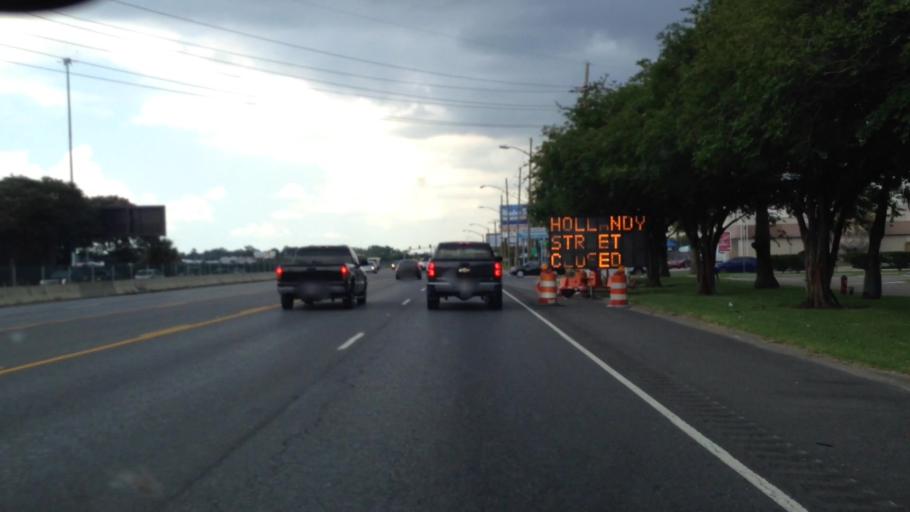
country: US
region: Louisiana
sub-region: Jefferson Parish
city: Kenner
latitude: 29.9823
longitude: -90.2572
